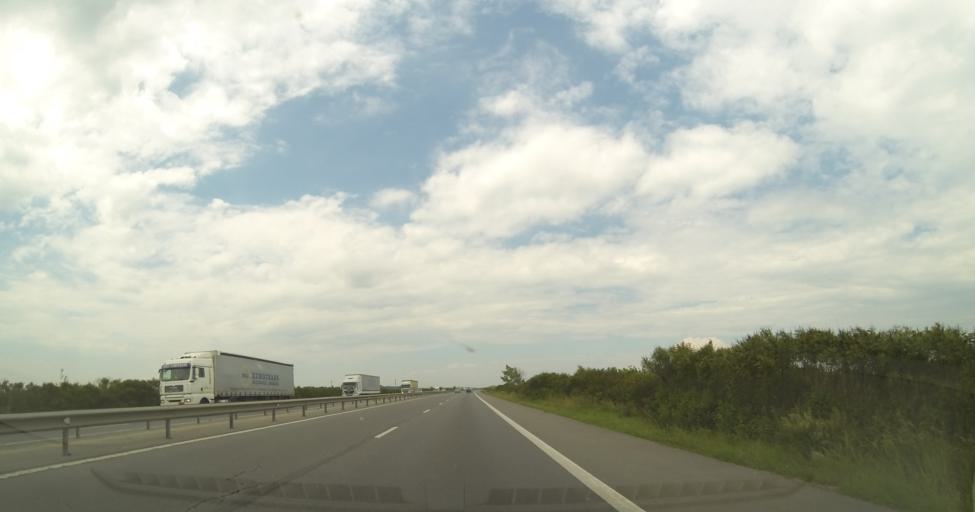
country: RO
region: Dambovita
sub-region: Comuna Corbii Mari
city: Corbii Mari
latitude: 44.5508
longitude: 25.5048
